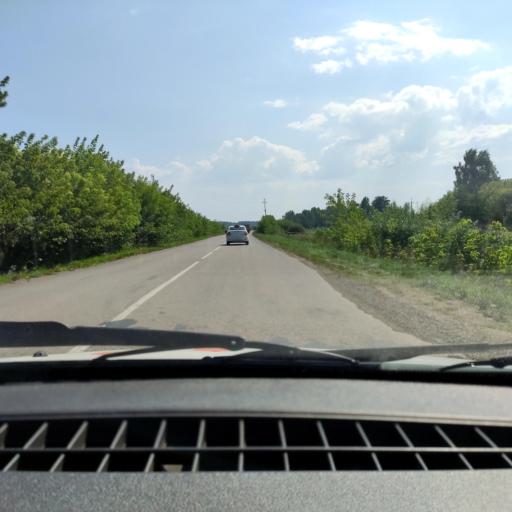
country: RU
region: Bashkortostan
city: Kudeyevskiy
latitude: 54.8308
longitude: 56.7930
